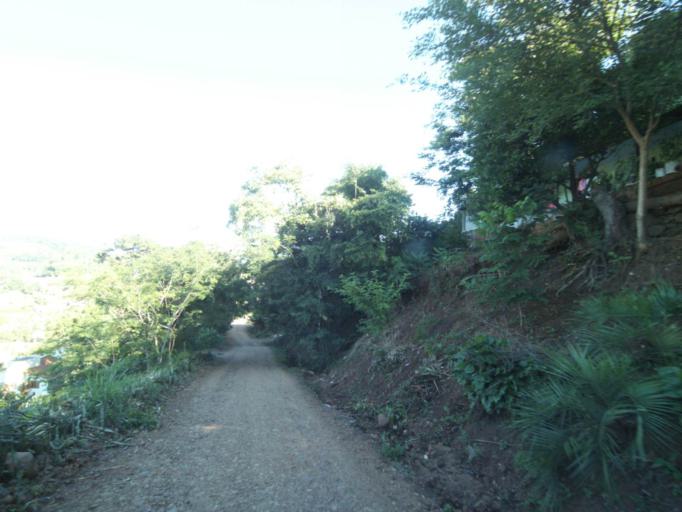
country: BR
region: Parana
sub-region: Ampere
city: Ampere
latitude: -26.1743
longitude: -53.3652
